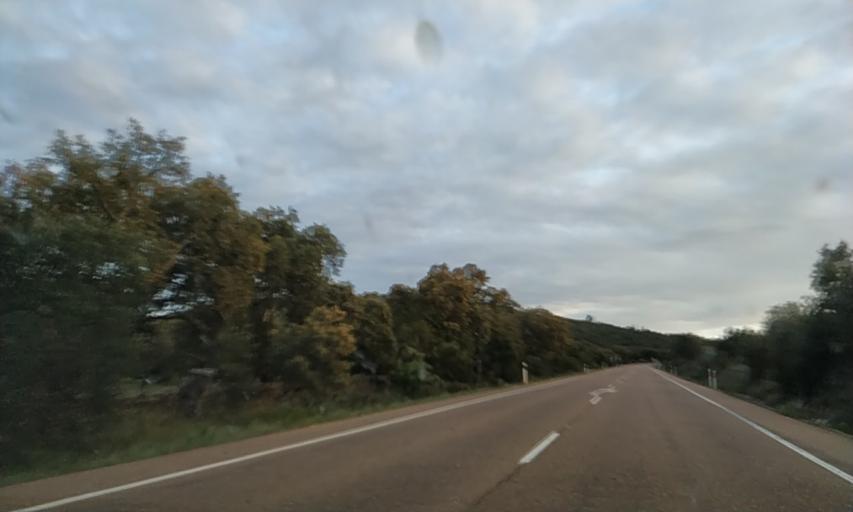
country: ES
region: Extremadura
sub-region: Provincia de Badajoz
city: Puebla de Obando
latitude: 39.1929
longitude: -6.5958
